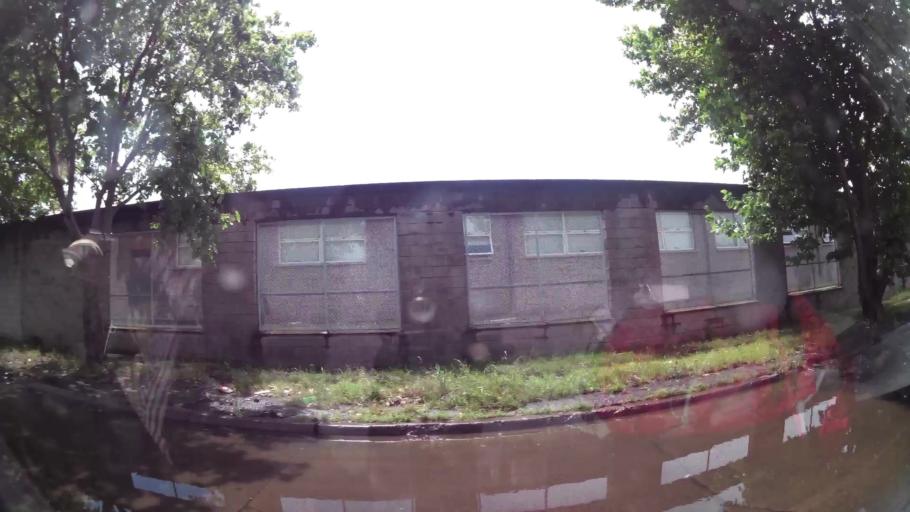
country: AR
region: Buenos Aires F.D.
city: Villa Lugano
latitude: -34.6589
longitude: -58.4630
